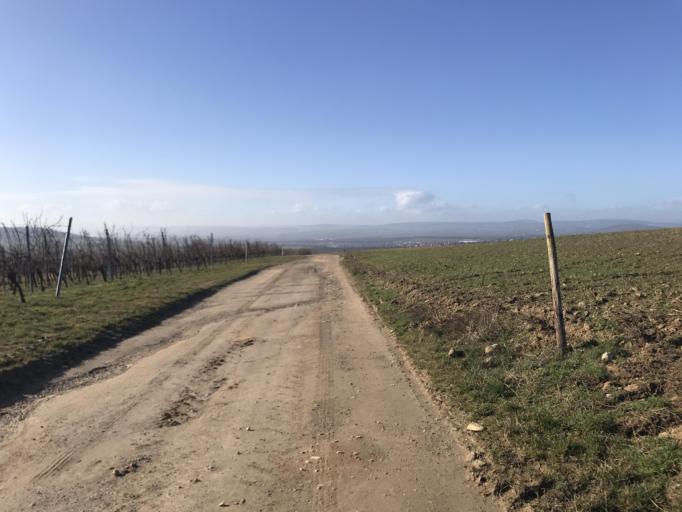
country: DE
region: Rheinland-Pfalz
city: Sankt Johann
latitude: 49.8799
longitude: 8.0233
